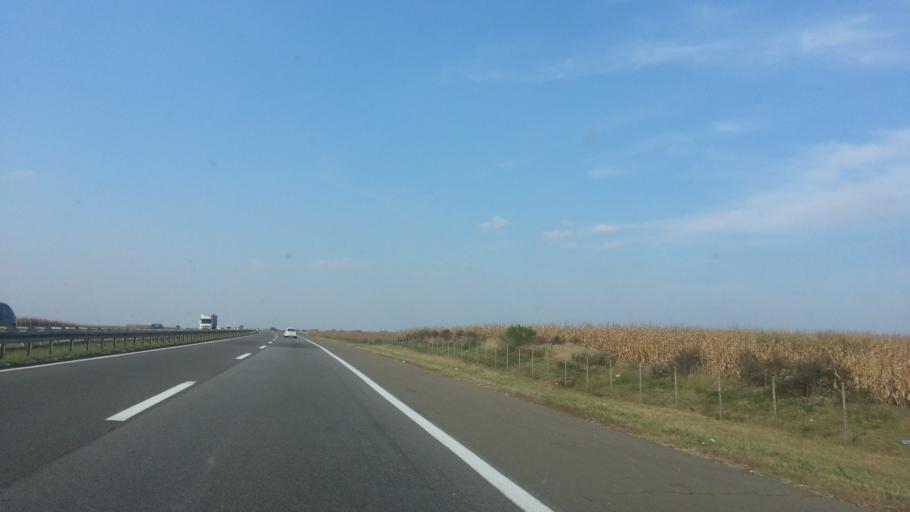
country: RS
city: Novi Banovci
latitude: 44.9216
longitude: 20.3040
